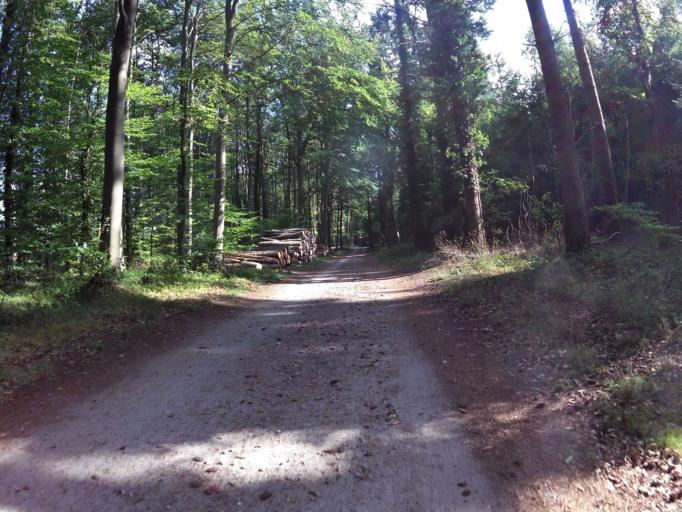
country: DE
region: Mecklenburg-Vorpommern
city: Koserow
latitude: 54.0467
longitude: 14.0218
